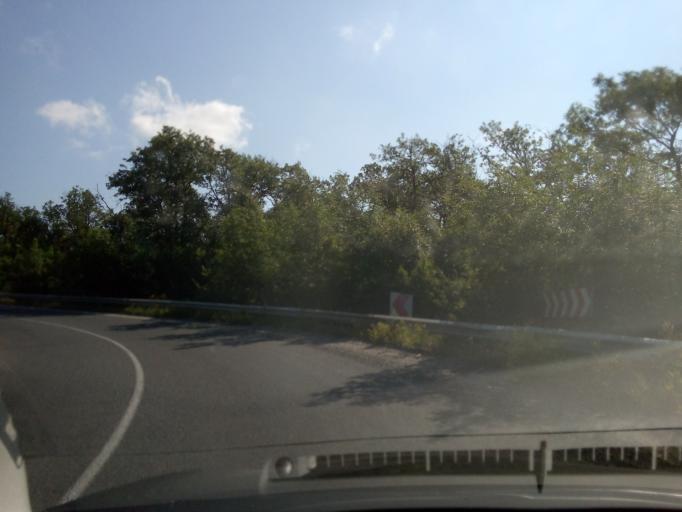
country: BG
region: Burgas
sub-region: Obshtina Nesebur
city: Sveti Vlas
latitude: 42.7468
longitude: 27.7530
